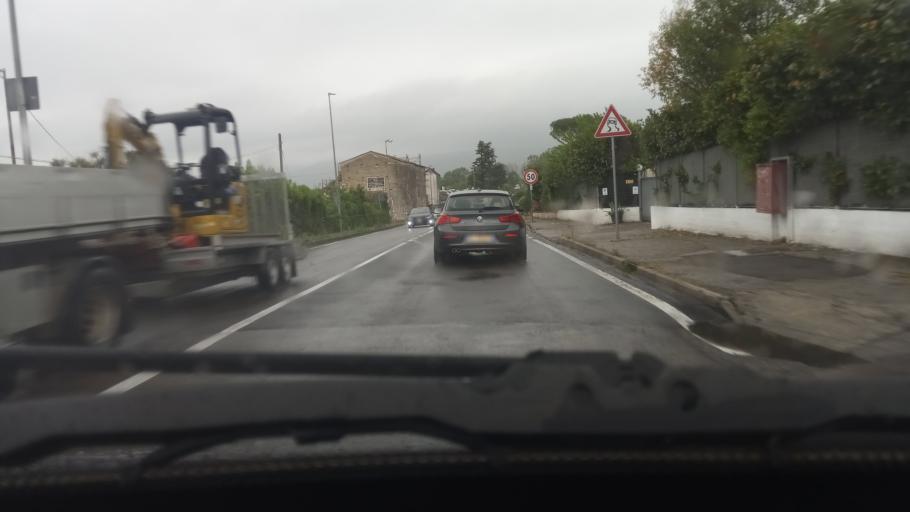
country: IT
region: Latium
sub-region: Provincia di Latina
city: Penitro
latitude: 41.2625
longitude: 13.6825
